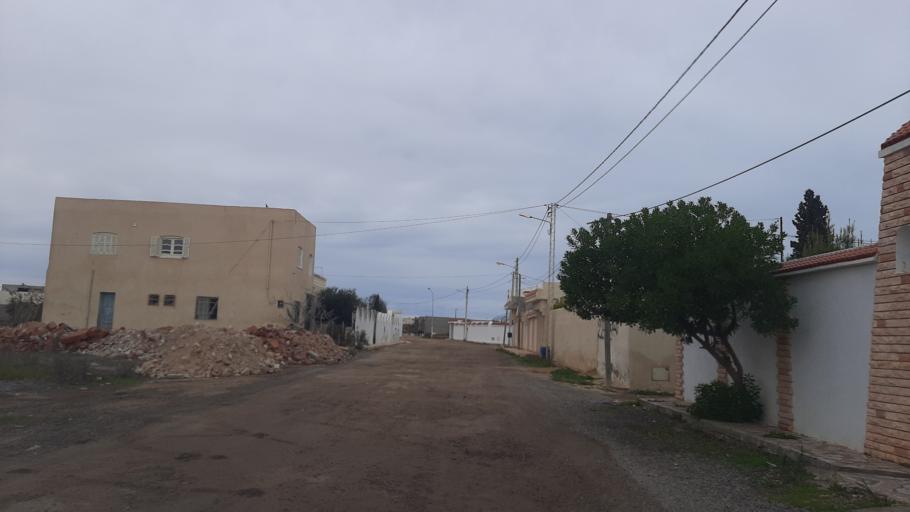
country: TN
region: Safaqis
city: Al Qarmadah
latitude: 34.7987
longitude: 10.8515
